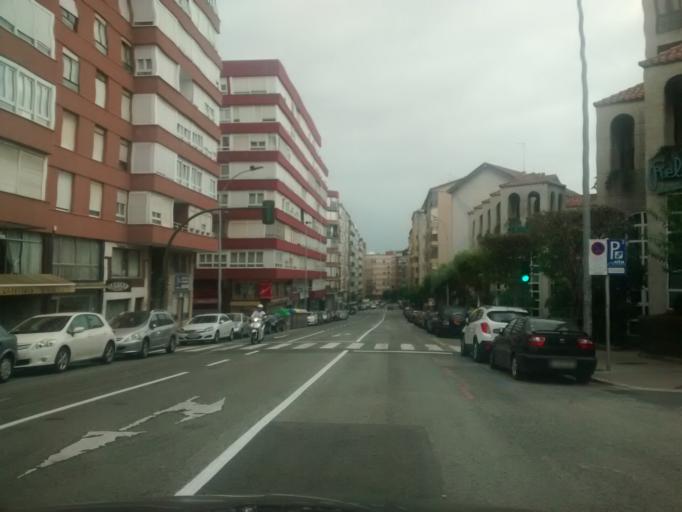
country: ES
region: Cantabria
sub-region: Provincia de Cantabria
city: Santander
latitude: 43.4618
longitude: -3.8243
